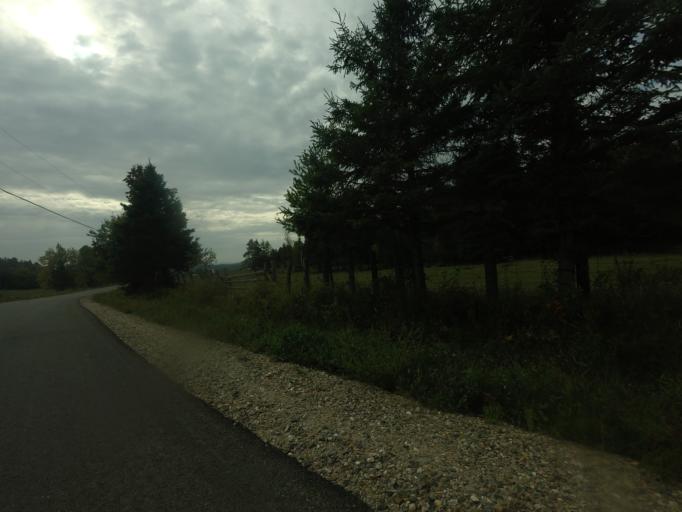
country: CA
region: Quebec
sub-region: Outaouais
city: Wakefield
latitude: 45.9857
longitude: -75.9410
